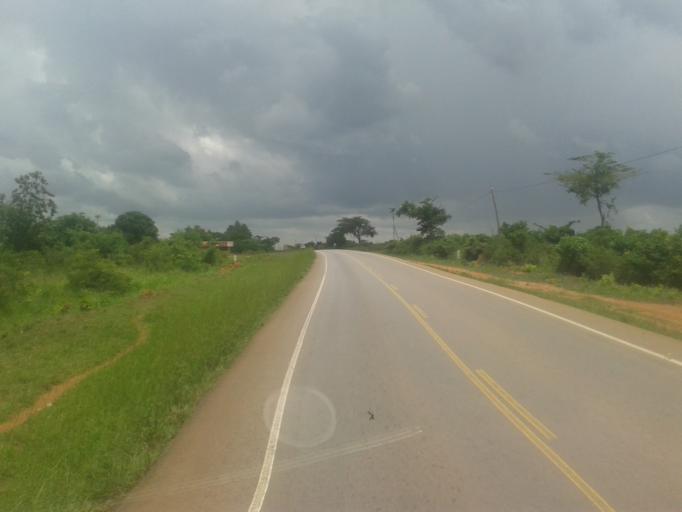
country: UG
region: Central Region
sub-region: Nakasongola District
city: Nakasongola
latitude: 1.2388
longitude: 32.4629
